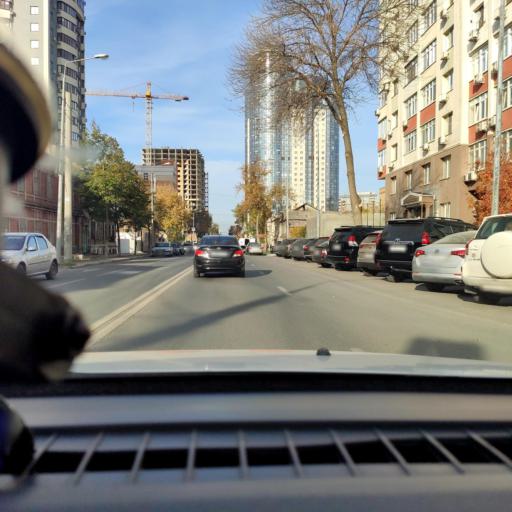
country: RU
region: Samara
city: Samara
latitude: 53.1950
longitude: 50.1142
